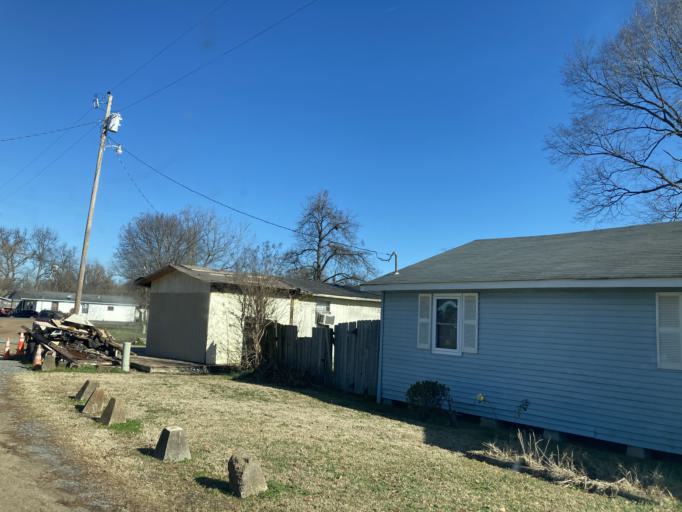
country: US
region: Mississippi
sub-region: Yazoo County
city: Yazoo City
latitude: 32.9772
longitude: -90.5944
